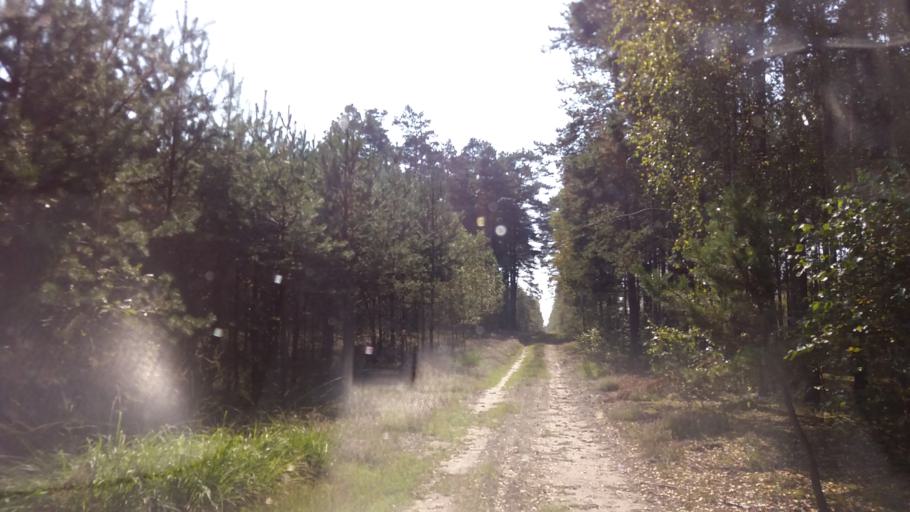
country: PL
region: West Pomeranian Voivodeship
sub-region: Powiat drawski
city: Kalisz Pomorski
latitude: 53.1308
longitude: 15.9402
